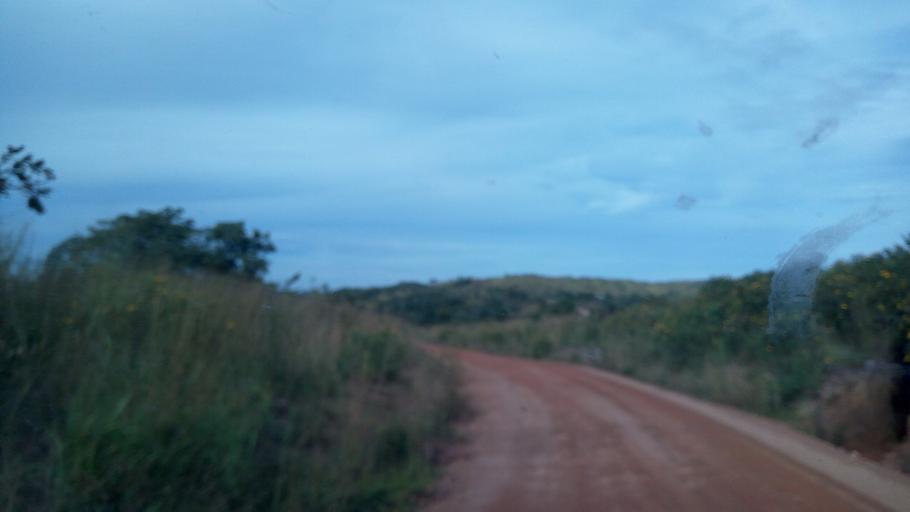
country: CD
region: Katanga
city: Kalemie
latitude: -6.2719
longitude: 29.0141
